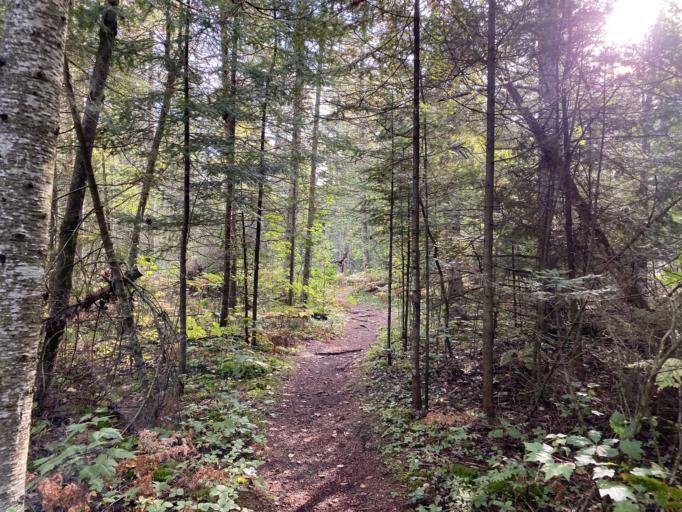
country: US
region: Michigan
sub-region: Mackinac County
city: Saint Ignace
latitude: 45.7427
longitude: -84.8938
